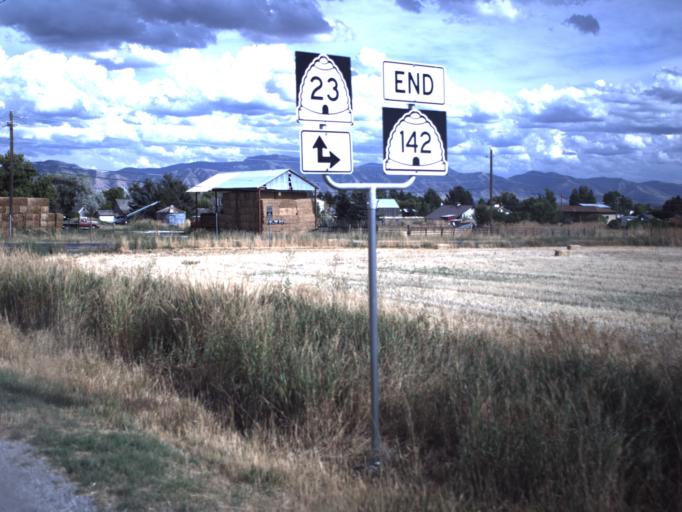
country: US
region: Utah
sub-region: Cache County
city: Benson
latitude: 41.8626
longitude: -112.0005
